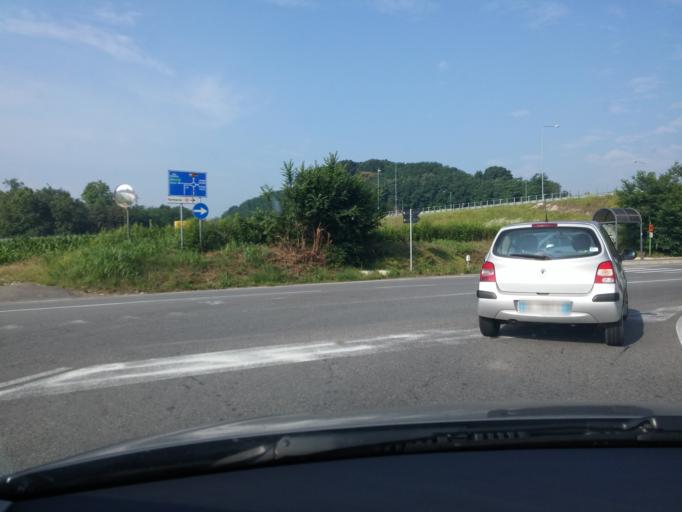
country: IT
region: Lombardy
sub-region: Provincia di Como
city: Fino Mornasco
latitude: 45.7492
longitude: 9.0393
